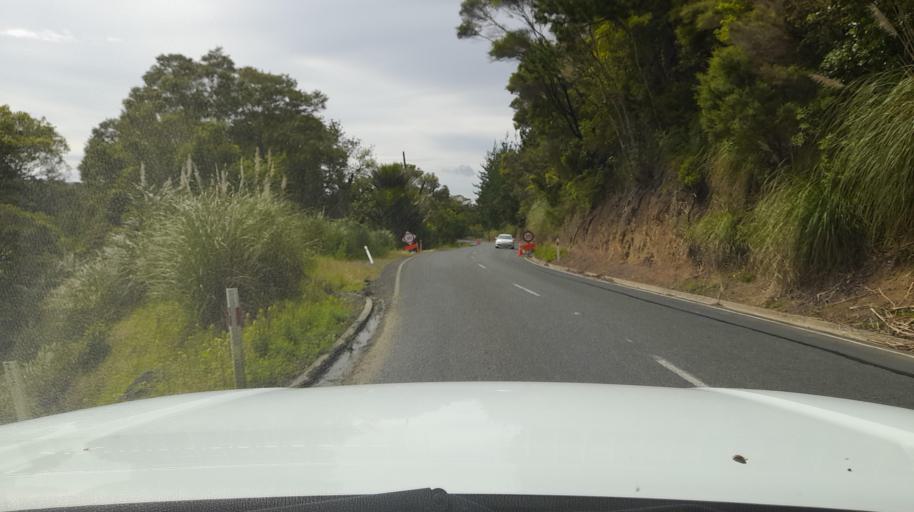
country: NZ
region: Northland
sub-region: Far North District
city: Taipa
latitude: -35.2532
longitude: 173.5331
